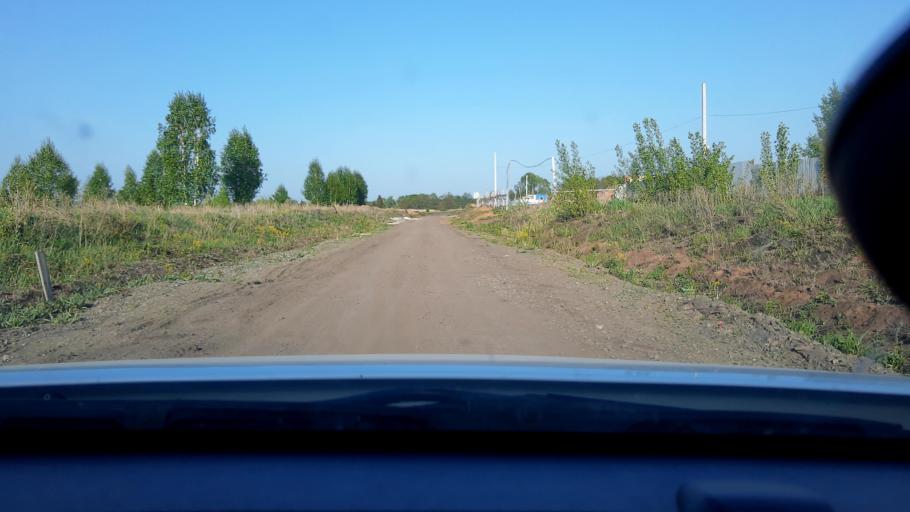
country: RU
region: Bashkortostan
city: Mikhaylovka
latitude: 54.7398
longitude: 55.8207
